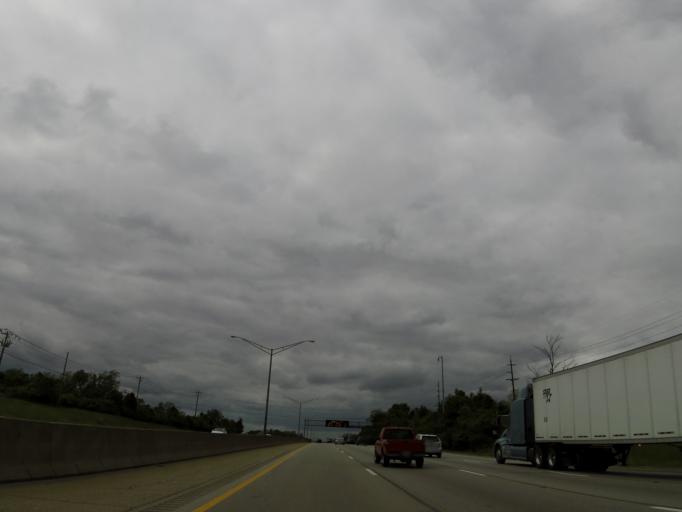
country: US
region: Kentucky
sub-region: Boone County
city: Walton
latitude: 38.9240
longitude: -84.6300
